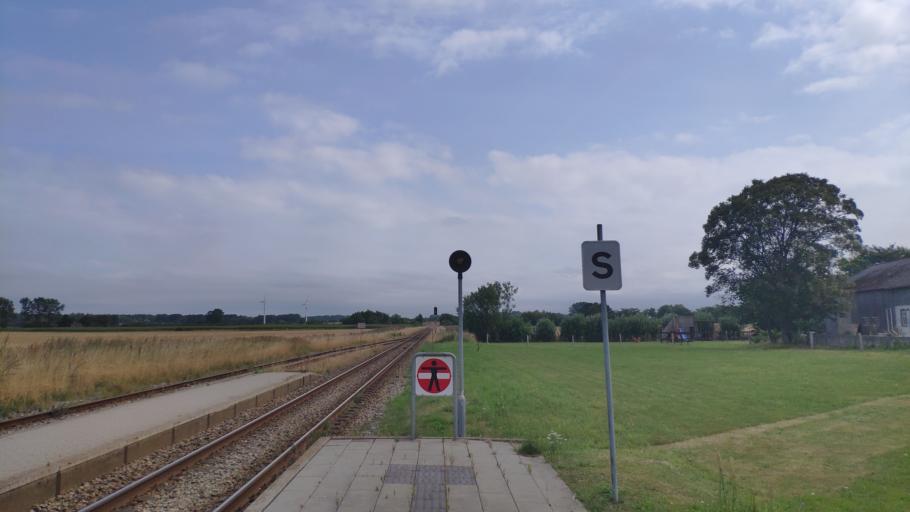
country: DK
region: Capital Region
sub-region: Halsnaes Kommune
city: Liseleje
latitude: 55.9771
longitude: 11.9145
